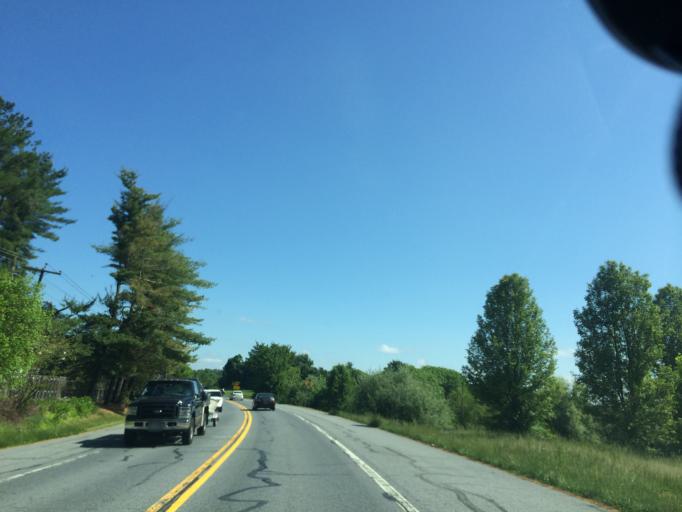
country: US
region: Maryland
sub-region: Baltimore County
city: Reisterstown
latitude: 39.5048
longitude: -76.8747
